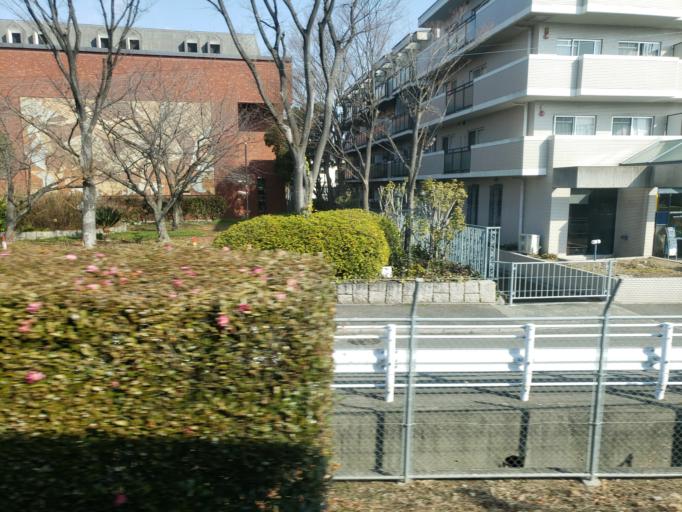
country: JP
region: Hyogo
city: Amagasaki
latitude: 34.7366
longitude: 135.4075
